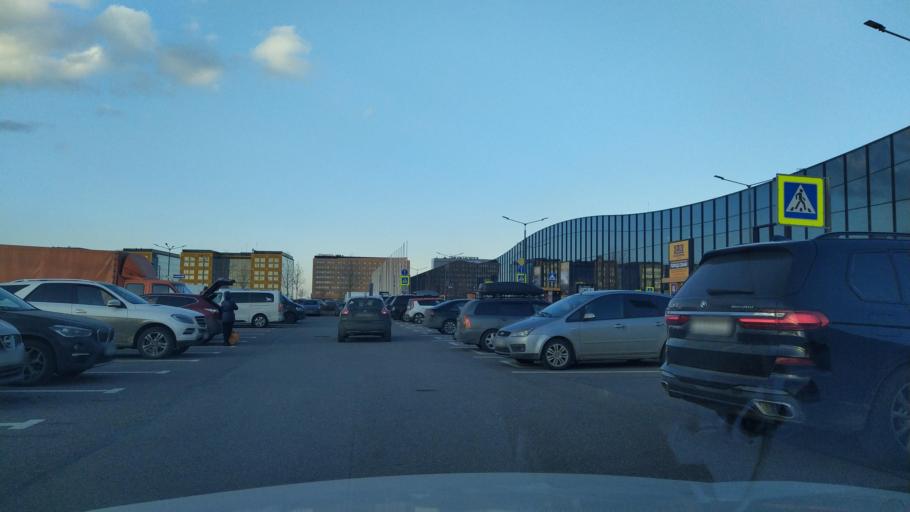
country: RU
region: St.-Petersburg
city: Aleksandrovskaya
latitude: 59.7601
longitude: 30.3515
